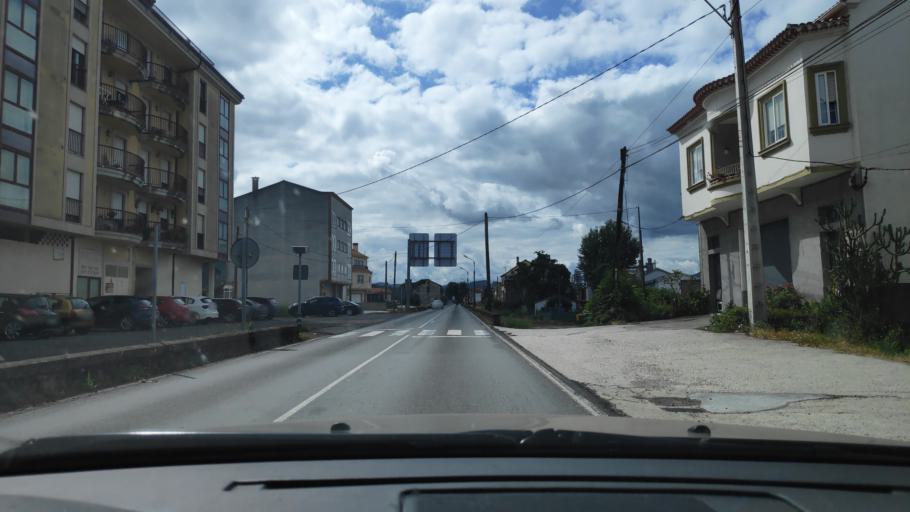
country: ES
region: Galicia
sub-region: Provincia da Coruna
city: Padron
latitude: 42.7287
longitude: -8.6572
